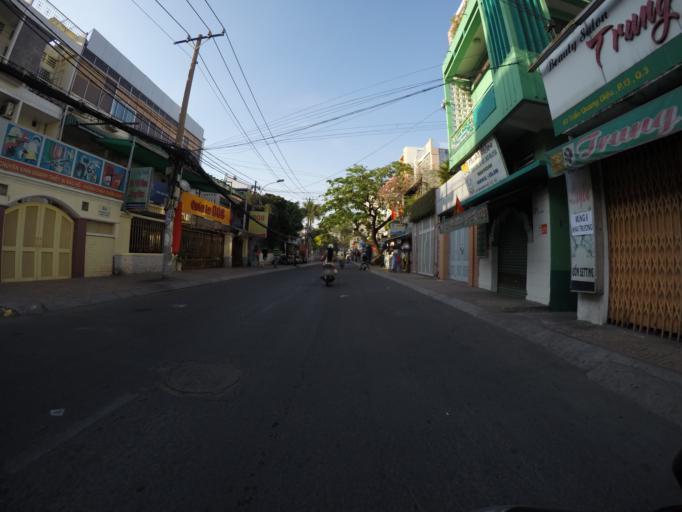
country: VN
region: Ho Chi Minh City
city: Quan Phu Nhuan
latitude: 10.7862
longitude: 106.6784
